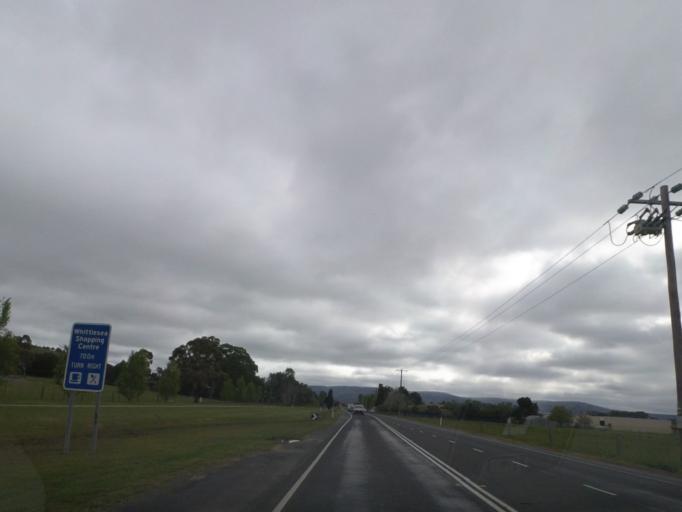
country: AU
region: Victoria
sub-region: Whittlesea
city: Whittlesea
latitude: -37.5207
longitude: 145.1133
